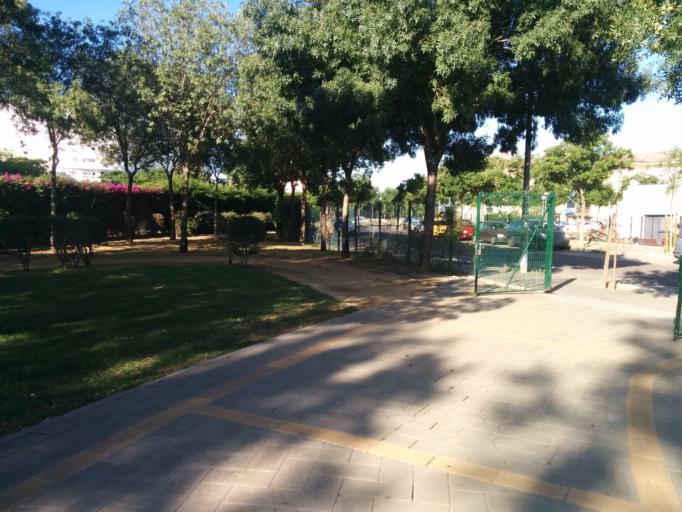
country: ES
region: Andalusia
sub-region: Provincia de Sevilla
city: Sevilla
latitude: 37.4091
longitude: -5.9160
